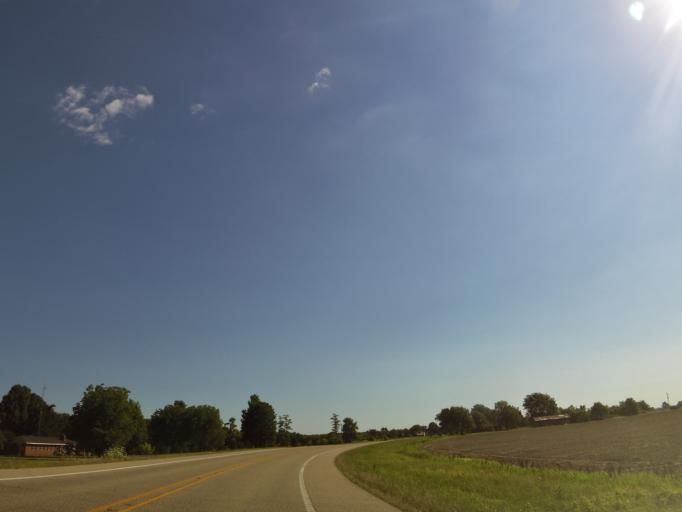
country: US
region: Arkansas
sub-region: Clay County
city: Corning
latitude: 36.4299
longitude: -90.4735
